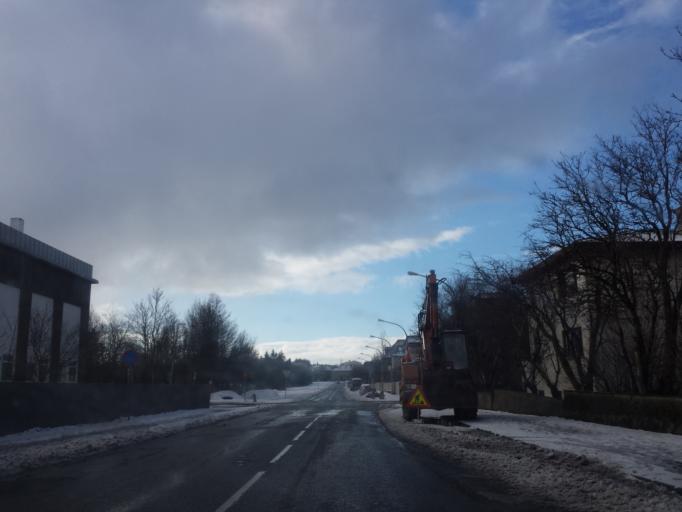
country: IS
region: Capital Region
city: Reykjavik
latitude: 64.1394
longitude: -21.9159
